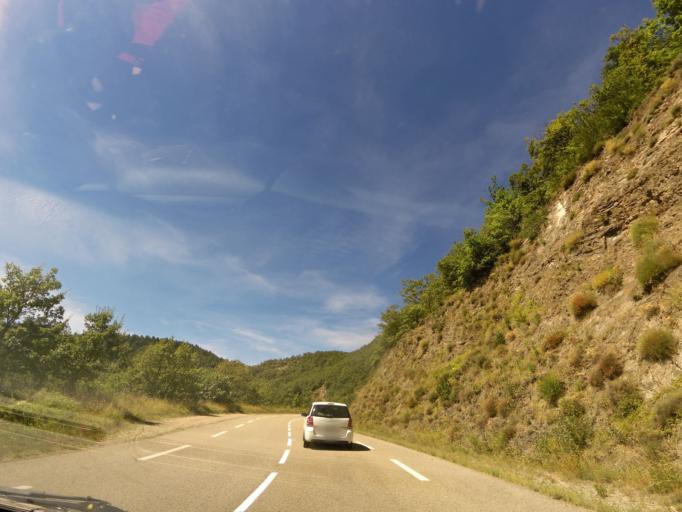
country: FR
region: Languedoc-Roussillon
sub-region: Departement du Gard
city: Le Vigan
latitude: 43.9739
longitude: 3.4574
